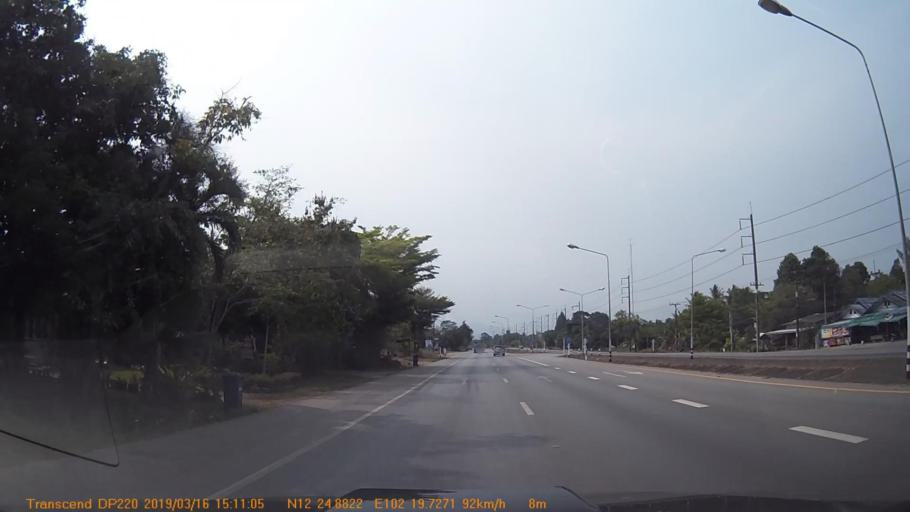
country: TH
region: Chanthaburi
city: Khlung
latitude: 12.4149
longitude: 102.3286
